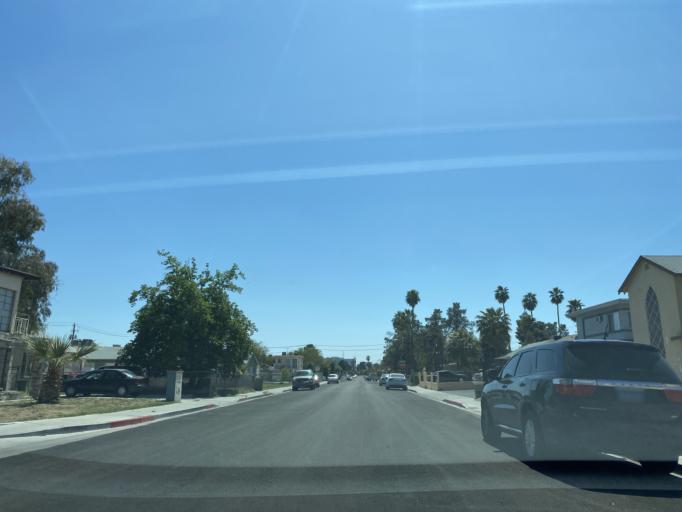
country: US
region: Nevada
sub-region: Clark County
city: Las Vegas
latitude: 36.1635
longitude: -115.1357
